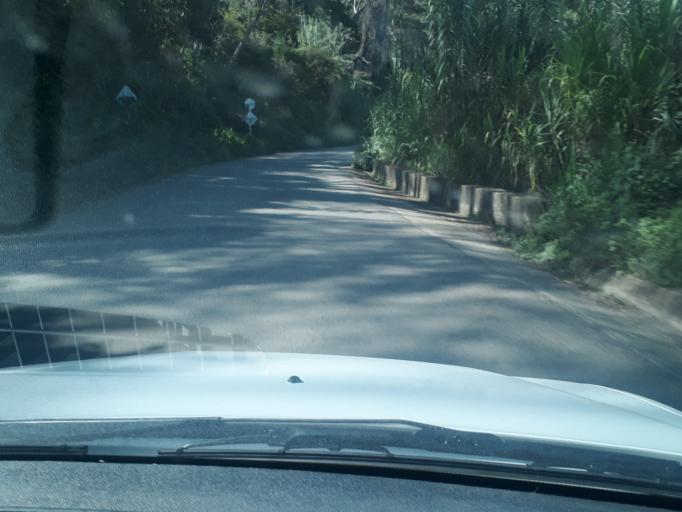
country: CO
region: Santander
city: Velez
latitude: 6.0274
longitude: -73.6547
